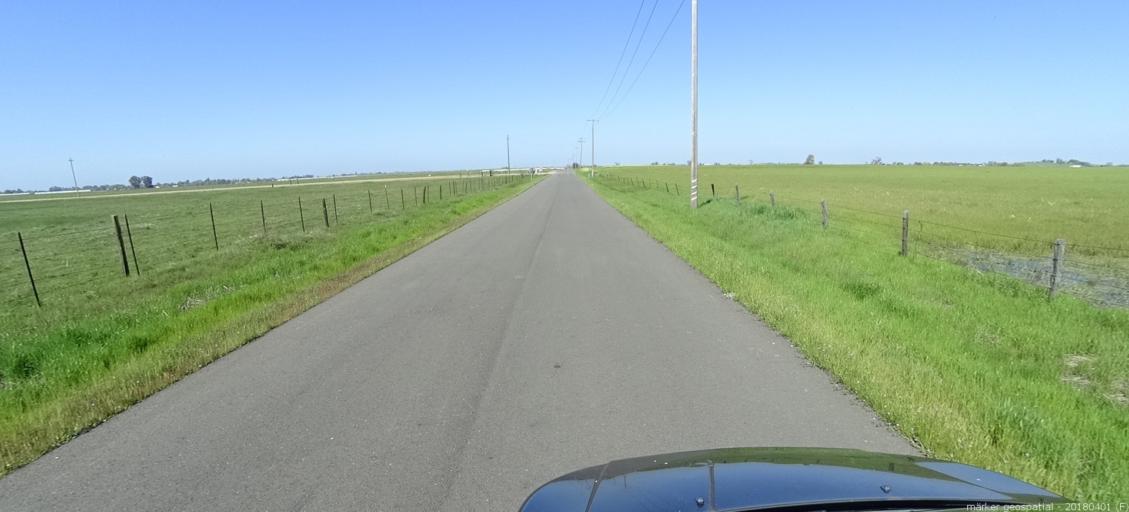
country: US
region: California
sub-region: Sacramento County
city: Rancho Murieta
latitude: 38.4655
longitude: -121.1431
